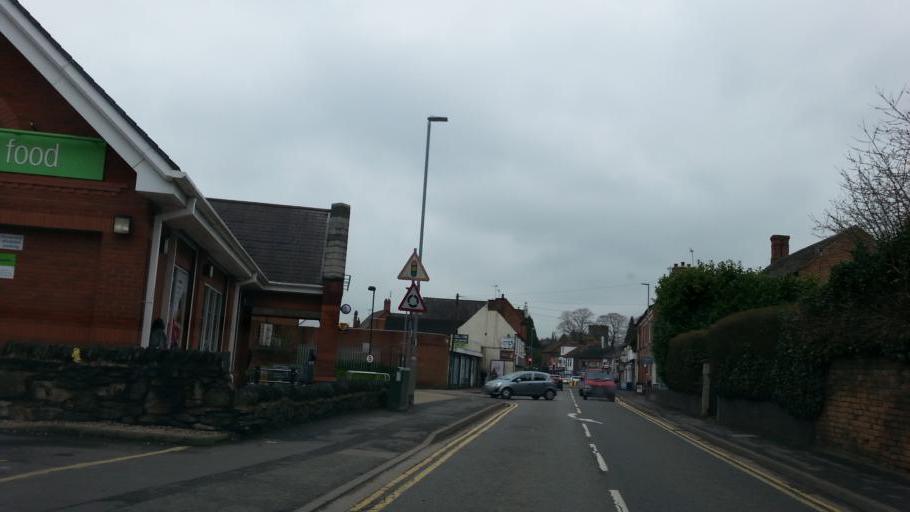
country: GB
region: England
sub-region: Leicestershire
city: Anstey
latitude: 52.6734
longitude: -1.1851
